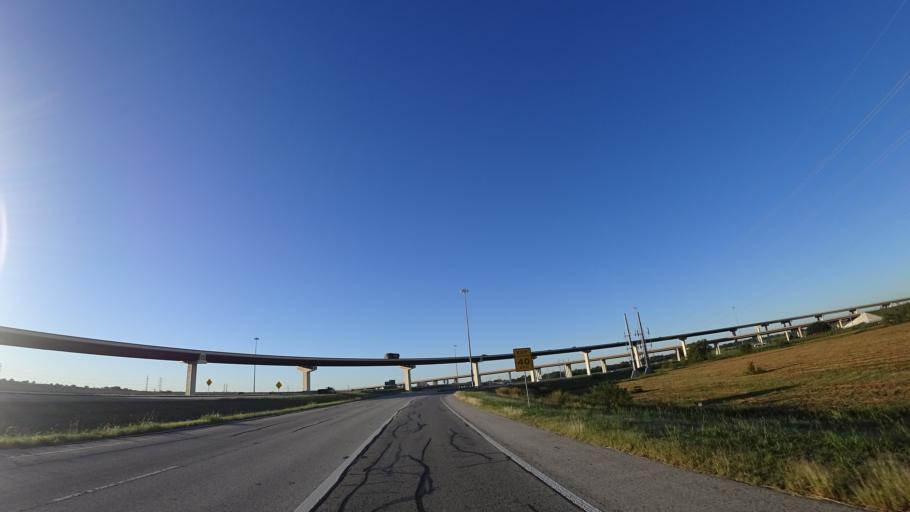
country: US
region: Texas
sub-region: Travis County
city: Hornsby Bend
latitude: 30.1988
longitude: -97.6233
